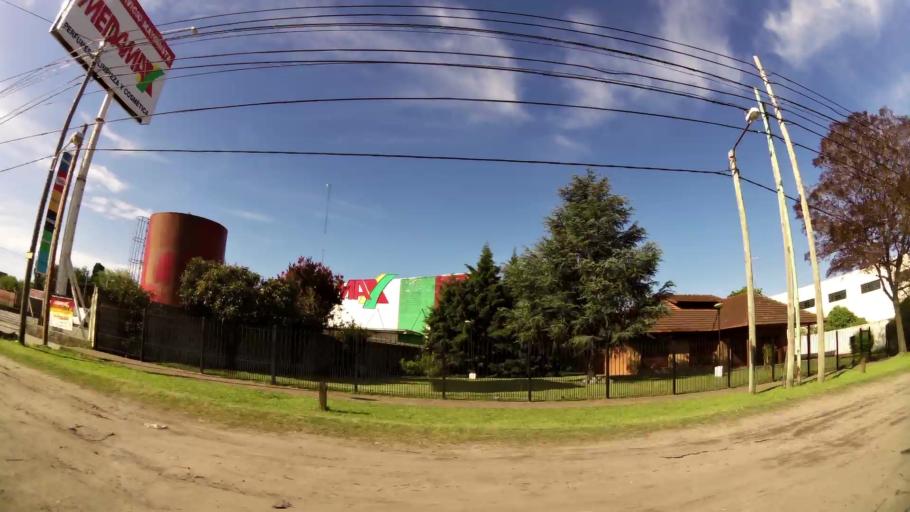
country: AR
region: Buenos Aires
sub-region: Partido de Quilmes
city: Quilmes
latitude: -34.7913
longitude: -58.2432
